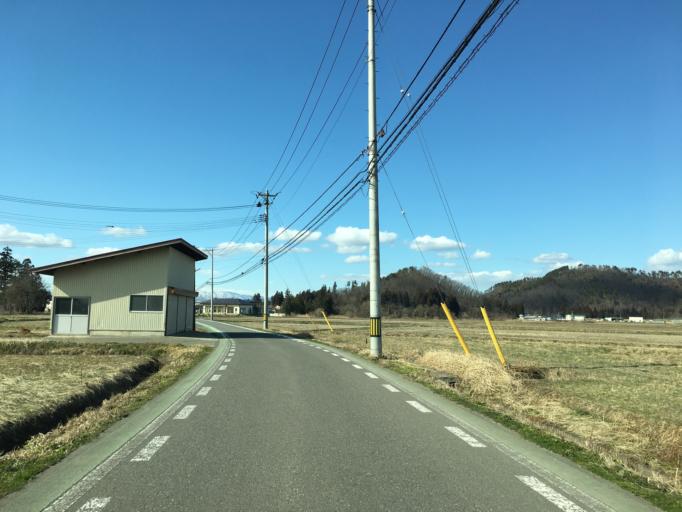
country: JP
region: Yamagata
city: Yonezawa
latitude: 37.9310
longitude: 140.1430
